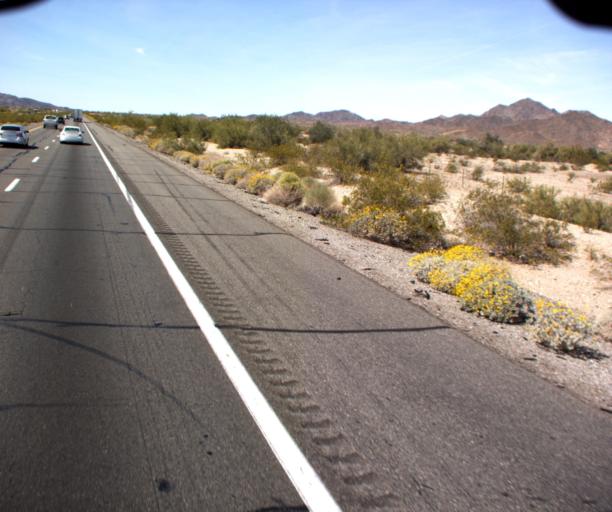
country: US
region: Arizona
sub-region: La Paz County
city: Quartzsite
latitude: 33.6530
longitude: -114.2897
